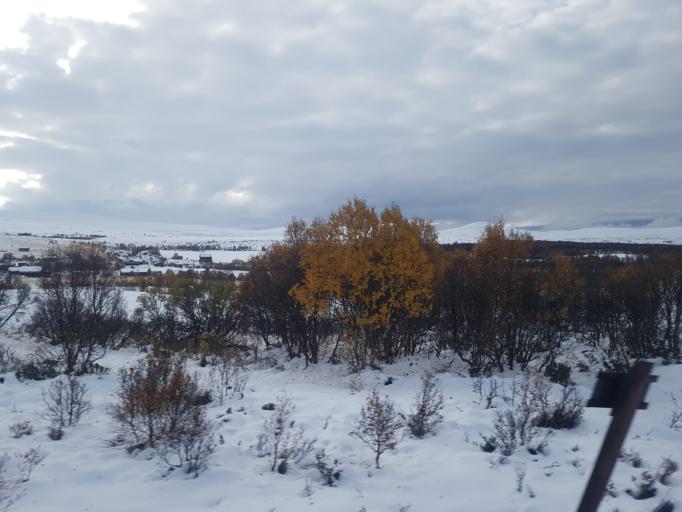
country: NO
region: Oppland
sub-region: Dovre
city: Dombas
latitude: 62.0996
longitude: 9.2311
